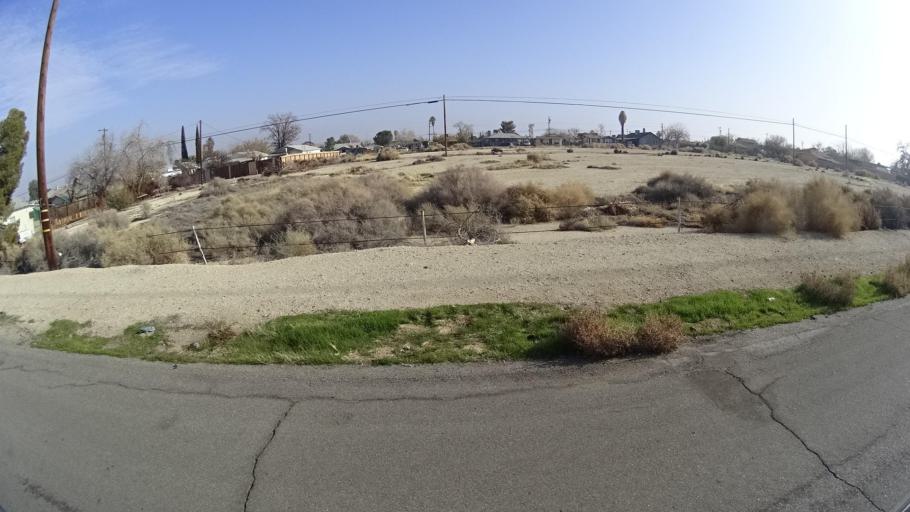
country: US
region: California
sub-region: Kern County
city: Ford City
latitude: 35.1582
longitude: -119.4653
